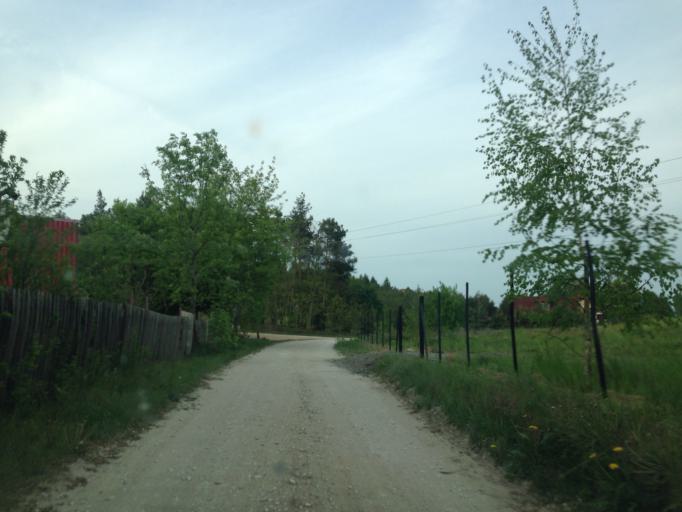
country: PL
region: Kujawsko-Pomorskie
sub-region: Powiat brodnicki
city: Brodnica
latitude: 53.3250
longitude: 19.3594
